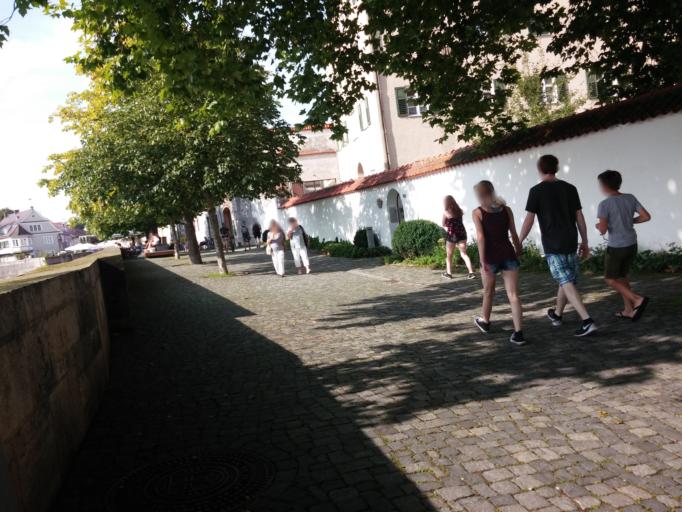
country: DE
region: Bavaria
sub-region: Upper Bavaria
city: Landsberg am Lech
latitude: 48.0482
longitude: 10.8756
